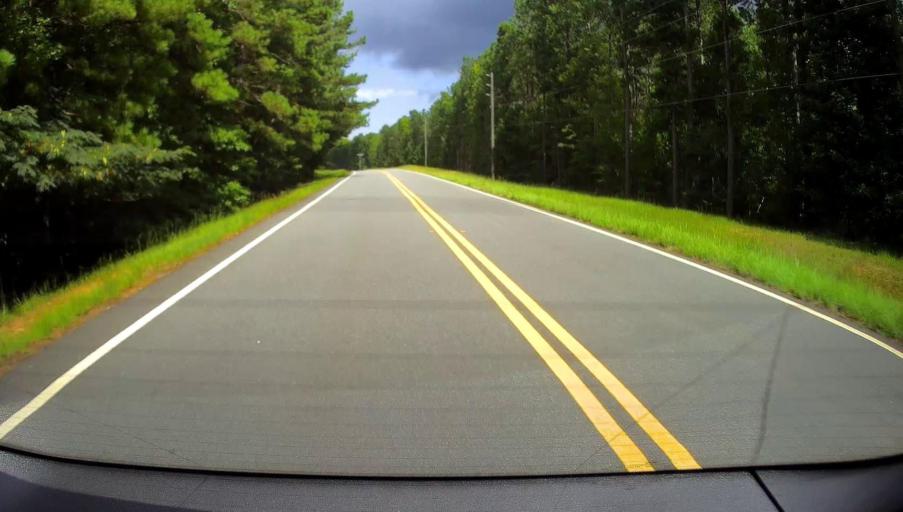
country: US
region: Georgia
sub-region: Monroe County
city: Forsyth
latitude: 32.8799
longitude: -83.9526
